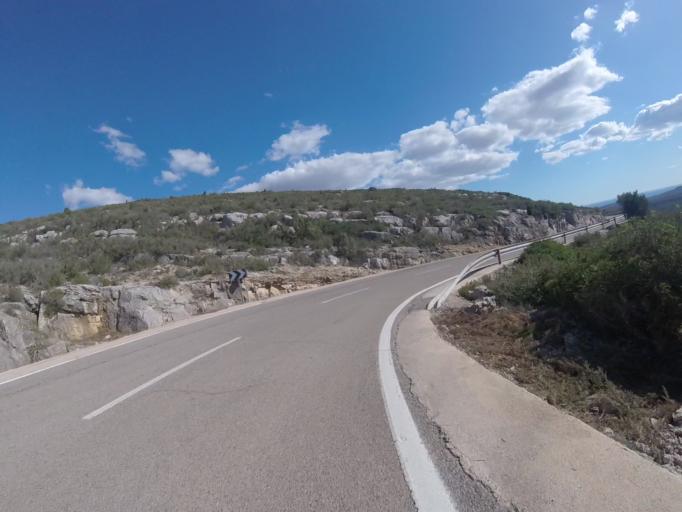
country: ES
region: Valencia
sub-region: Provincia de Castello
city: Alcala de Xivert
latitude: 40.2943
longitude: 0.1807
